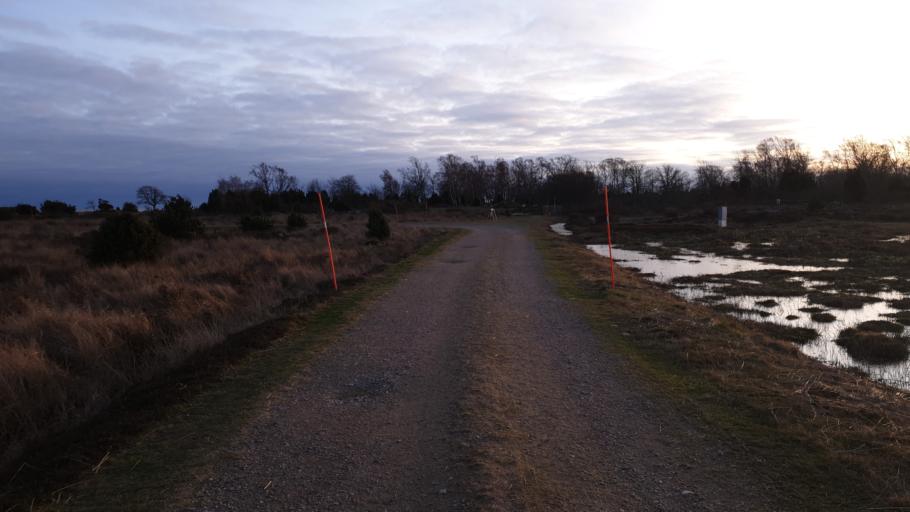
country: SE
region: Blekinge
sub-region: Karlskrona Kommun
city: Jaemjoe
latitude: 56.0787
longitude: 15.8464
